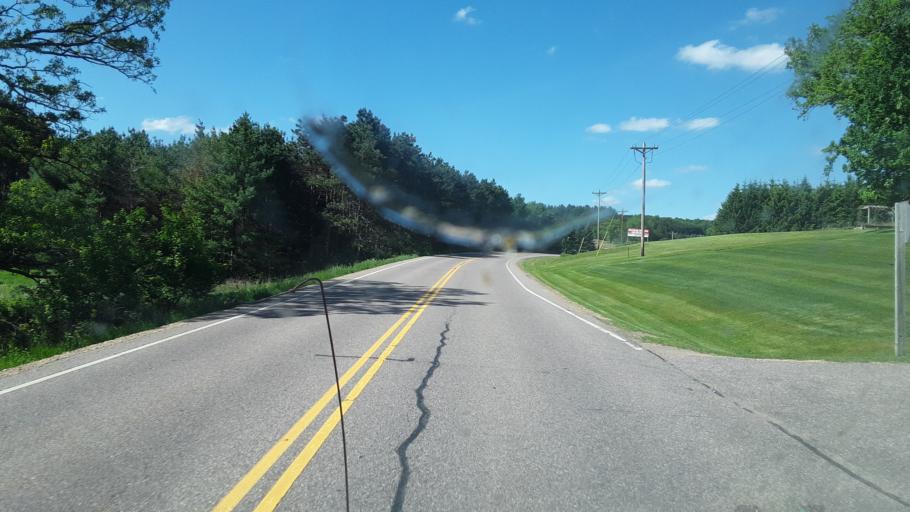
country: US
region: Wisconsin
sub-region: Sauk County
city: Reedsburg
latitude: 43.6047
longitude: -90.1243
